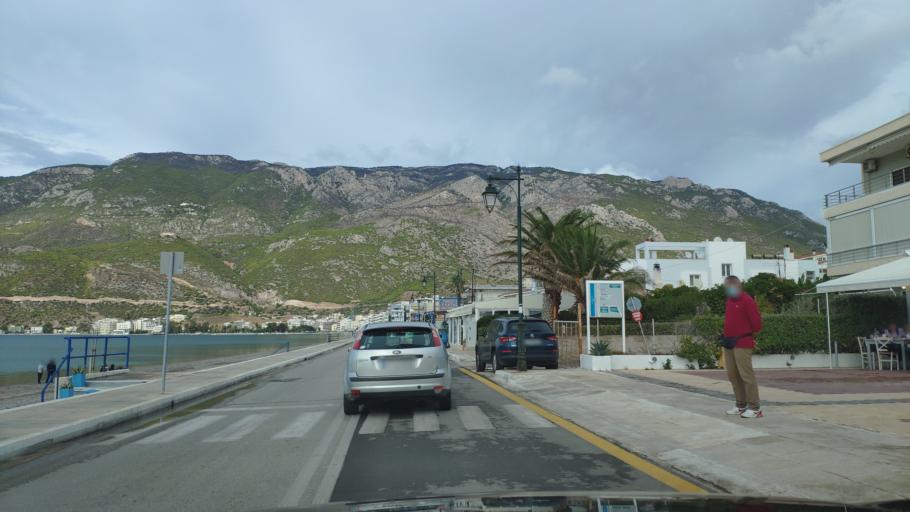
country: GR
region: Peloponnese
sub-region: Nomos Korinthias
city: Loutraki
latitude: 37.9674
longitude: 22.9725
